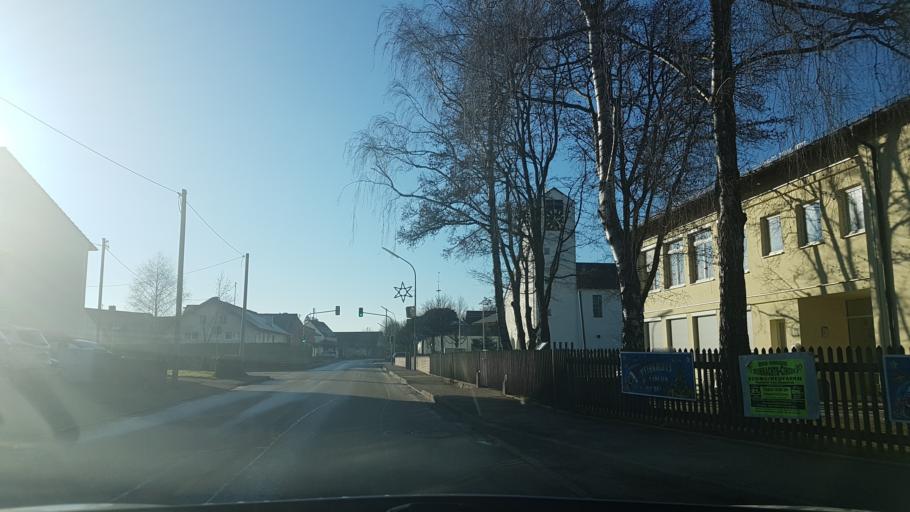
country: DE
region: Bavaria
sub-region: Upper Bavaria
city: Hallbergmoos
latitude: 48.3105
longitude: 11.7494
